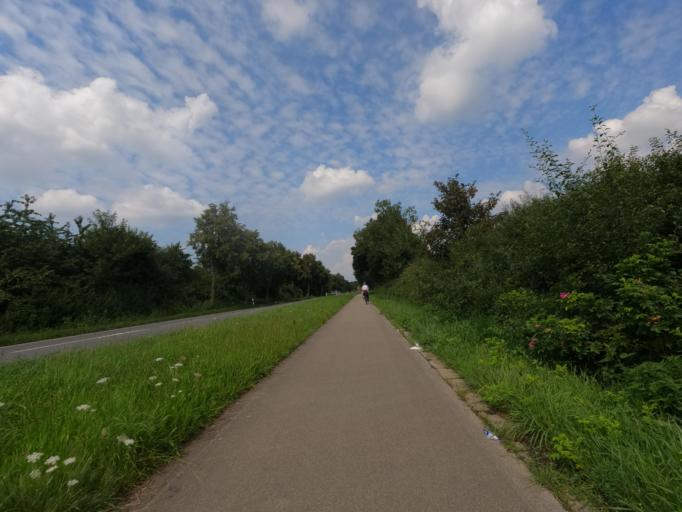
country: DE
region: North Rhine-Westphalia
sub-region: Regierungsbezirk Koln
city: Ubach-Palenberg
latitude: 50.9469
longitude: 6.1306
